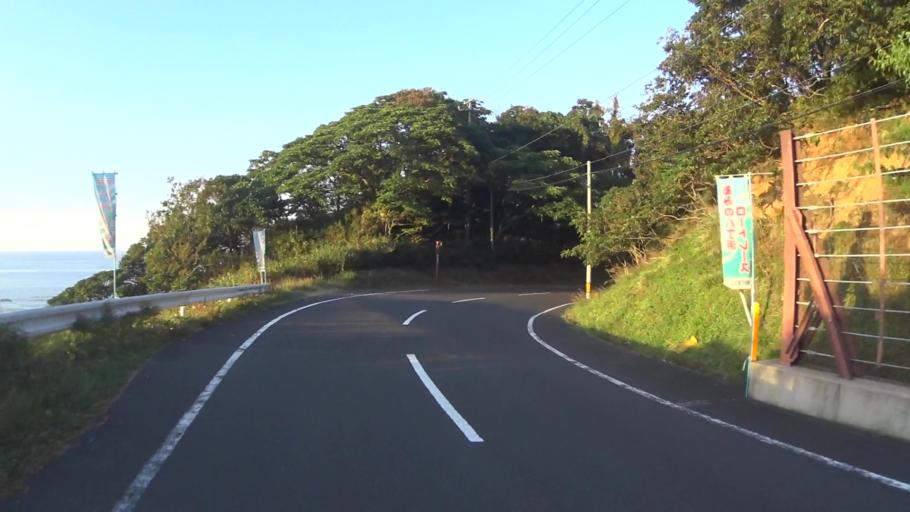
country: JP
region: Hyogo
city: Toyooka
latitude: 35.6916
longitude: 135.0025
